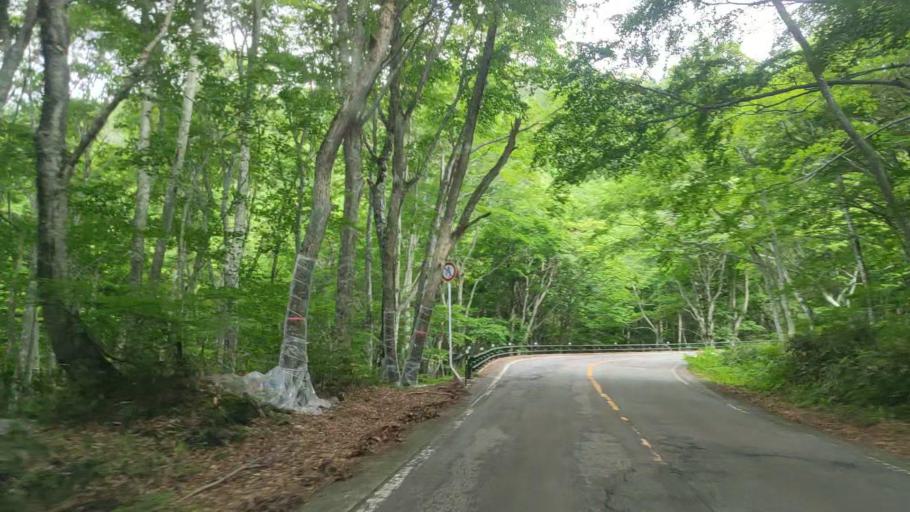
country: JP
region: Tottori
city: Yonago
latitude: 35.3470
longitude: 133.5539
